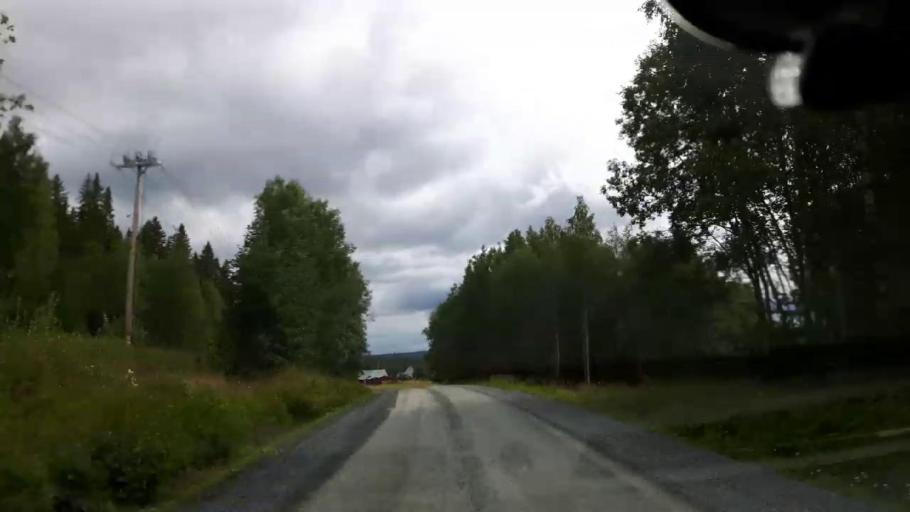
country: SE
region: Jaemtland
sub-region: Krokoms Kommun
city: Valla
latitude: 63.5873
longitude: 14.1509
